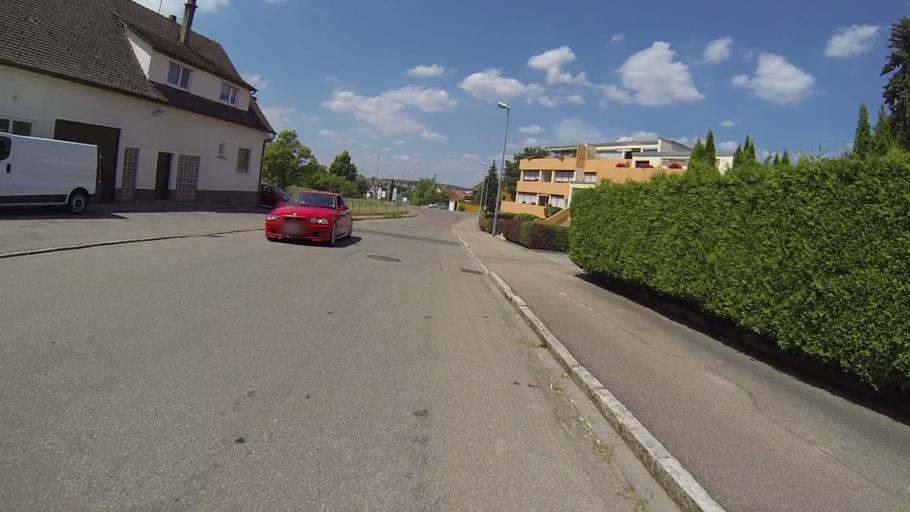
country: DE
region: Baden-Wuerttemberg
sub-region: Regierungsbezirk Stuttgart
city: Herbrechtingen
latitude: 48.6182
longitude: 10.1851
